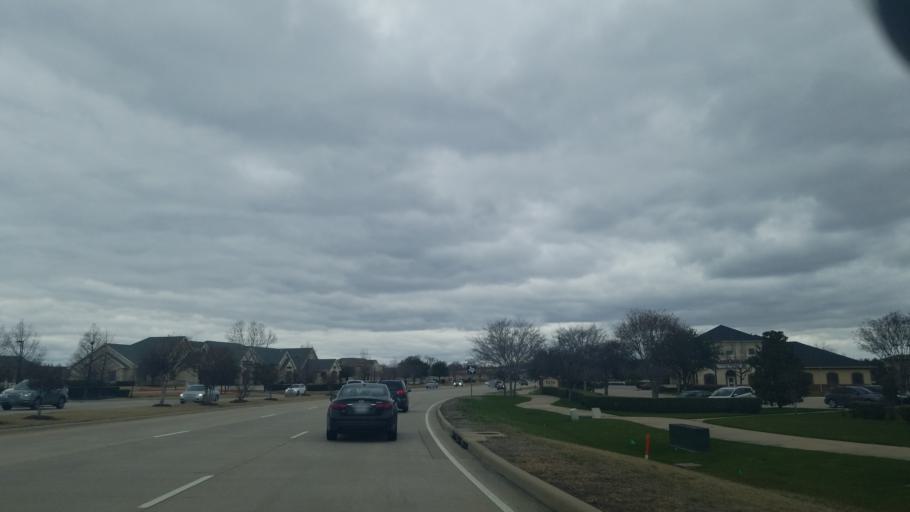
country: US
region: Texas
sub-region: Denton County
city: Double Oak
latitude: 33.0513
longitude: -97.0733
